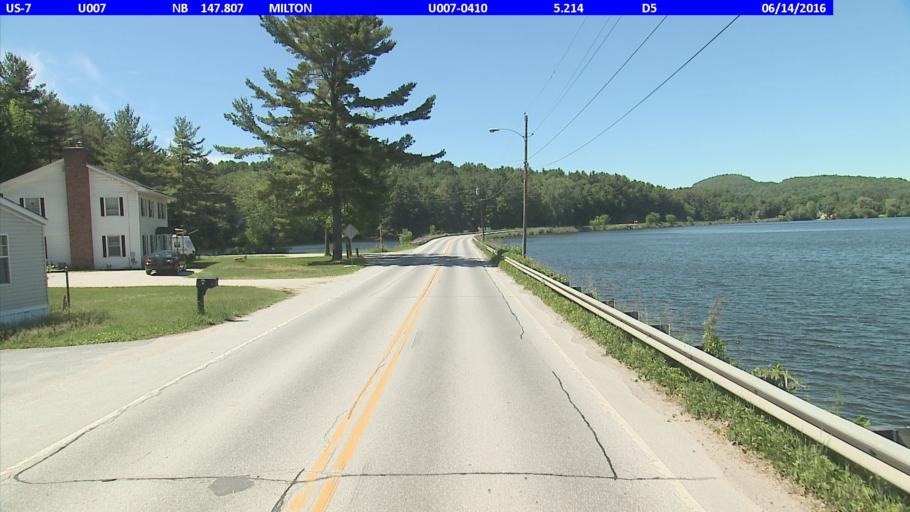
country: US
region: Vermont
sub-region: Chittenden County
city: Milton
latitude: 44.6422
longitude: -73.1149
